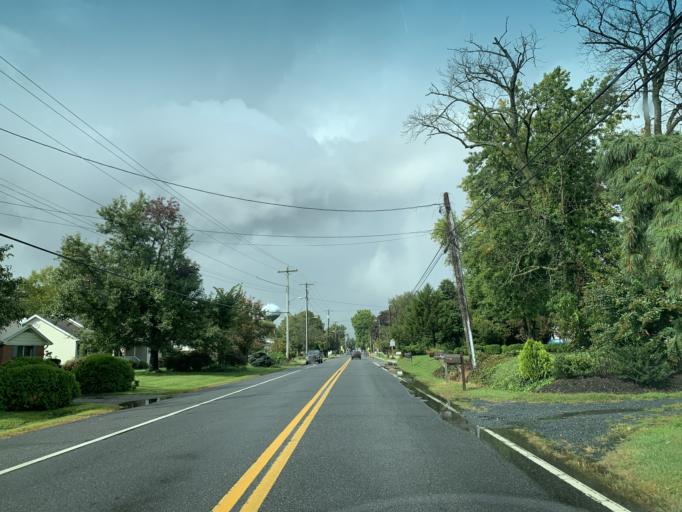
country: US
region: Maryland
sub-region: Queen Anne's County
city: Kingstown
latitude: 39.1815
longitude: -75.8578
